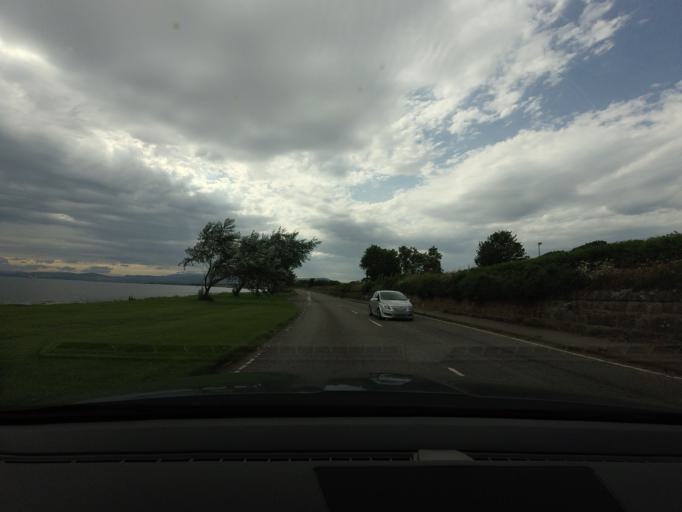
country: GB
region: Scotland
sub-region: Highland
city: Invergordon
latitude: 57.6912
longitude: -4.1880
